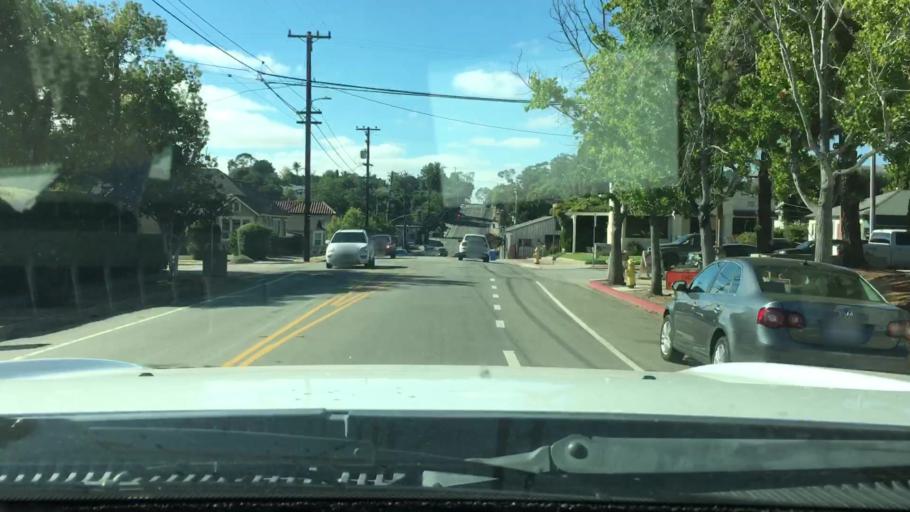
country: US
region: California
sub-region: San Luis Obispo County
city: San Luis Obispo
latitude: 35.2851
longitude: -120.6536
